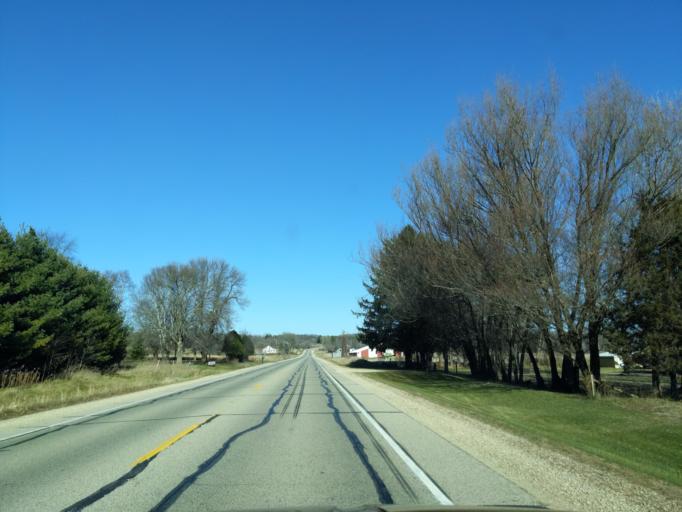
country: US
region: Wisconsin
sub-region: Waushara County
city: Wautoma
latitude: 44.0968
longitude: -89.2908
